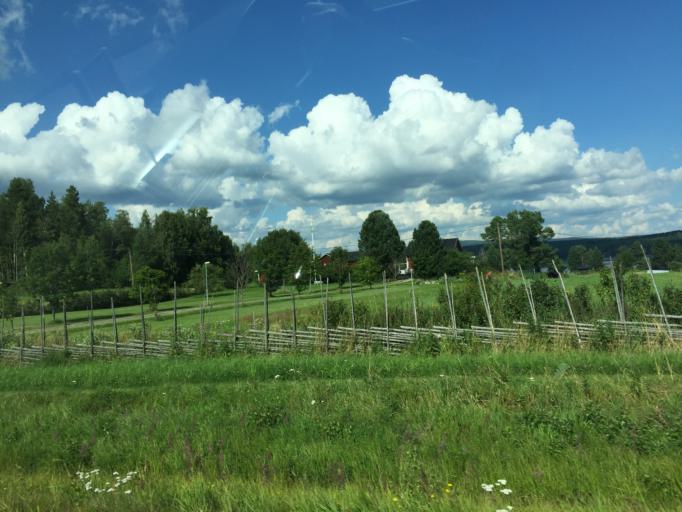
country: SE
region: Gaevleborg
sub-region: Bollnas Kommun
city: Bollnas
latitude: 61.3110
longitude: 16.4490
